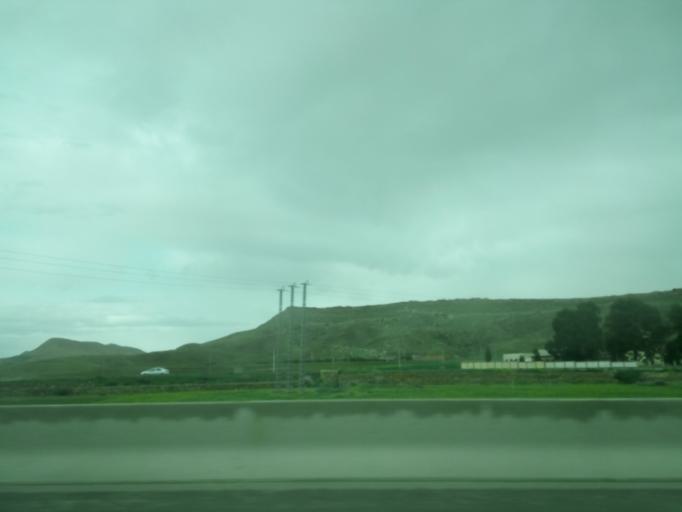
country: DZ
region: Medea
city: Ksar el Boukhari
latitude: 35.8231
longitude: 2.7689
